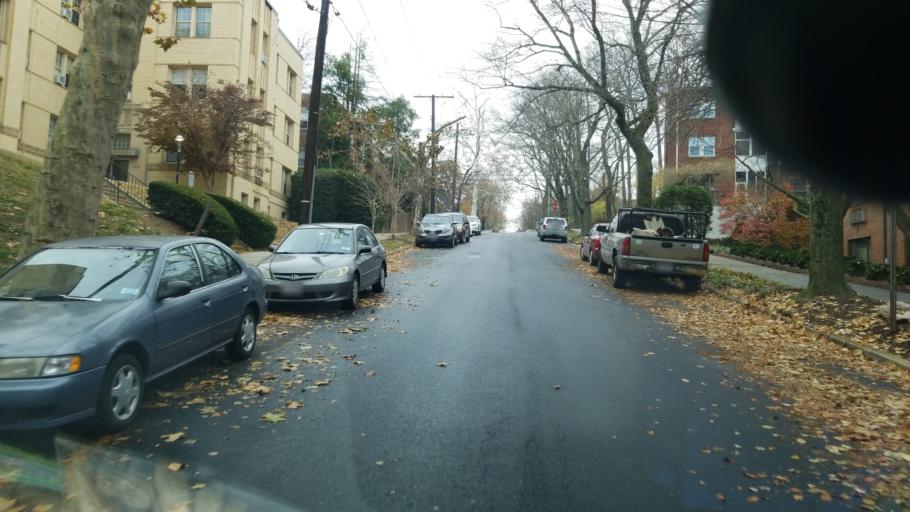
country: US
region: Maryland
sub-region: Montgomery County
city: Friendship Village
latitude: 38.9236
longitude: -77.0815
